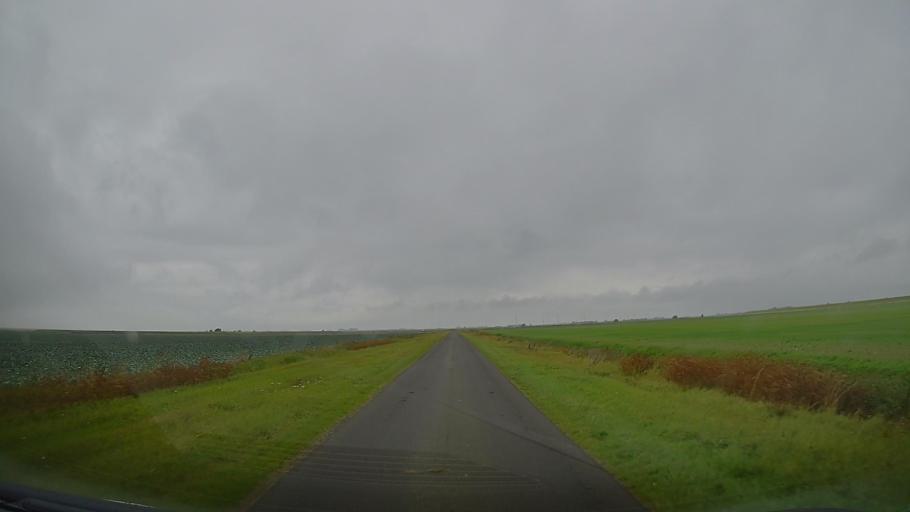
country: DE
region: Schleswig-Holstein
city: Friedrichsgabekoog
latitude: 54.1098
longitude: 8.9839
